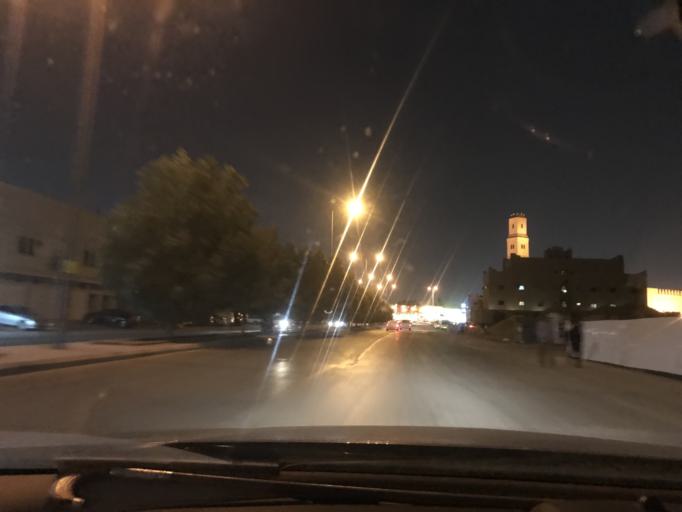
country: SA
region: Ar Riyad
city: Riyadh
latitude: 24.7481
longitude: 46.7588
